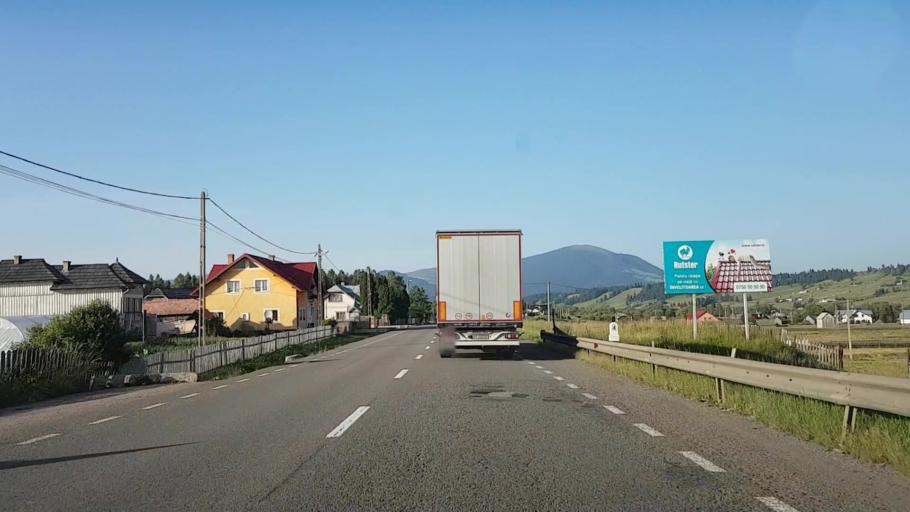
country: RO
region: Suceava
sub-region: Comuna Poiana Stampei
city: Poiana Stampei
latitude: 47.3305
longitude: 25.1542
